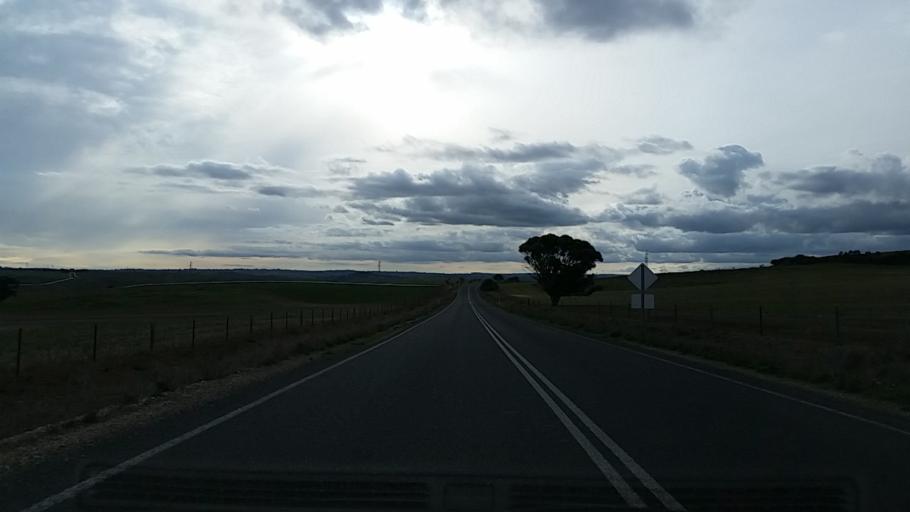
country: AU
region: South Australia
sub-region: Mount Barker
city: Callington
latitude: -35.0699
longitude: 139.0469
